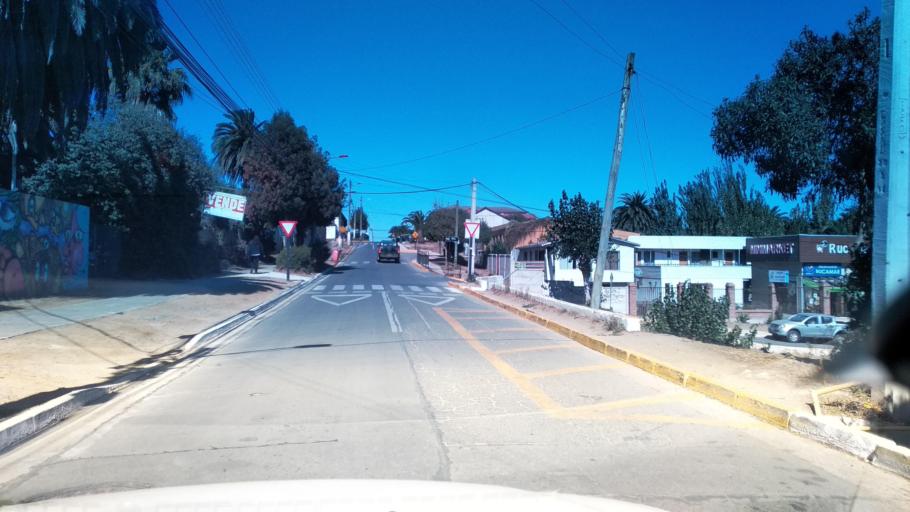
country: CL
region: O'Higgins
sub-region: Provincia de Colchagua
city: Santa Cruz
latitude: -34.3879
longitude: -72.0037
